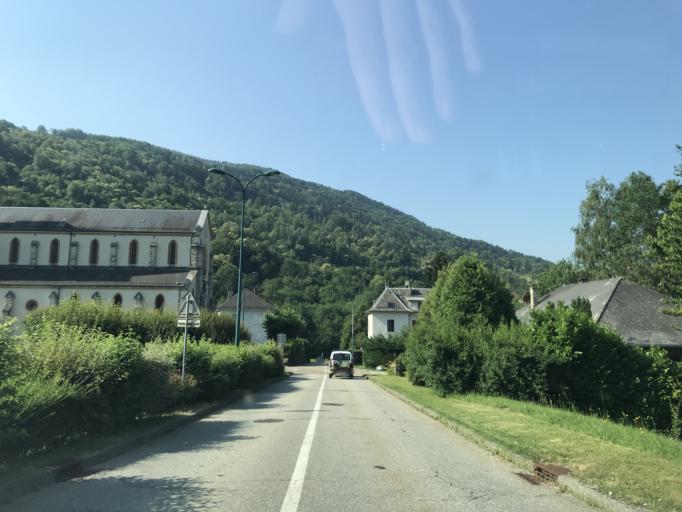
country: FR
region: Rhone-Alpes
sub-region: Departement de la Savoie
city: La Rochette
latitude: 45.4406
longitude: 6.1201
